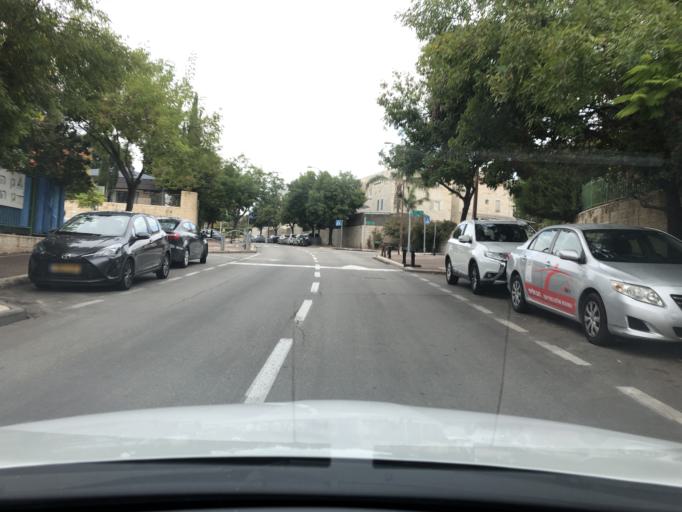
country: IL
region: Central District
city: Modiin
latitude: 31.9062
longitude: 35.0078
